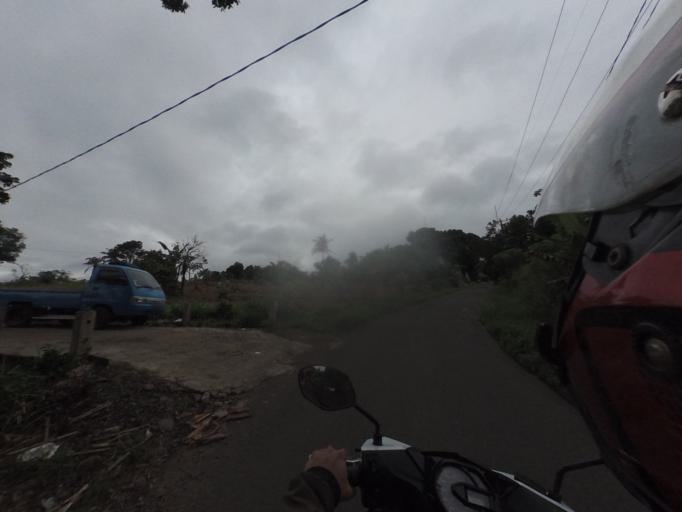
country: ID
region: West Java
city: Bogor
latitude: -6.6538
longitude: 106.7286
